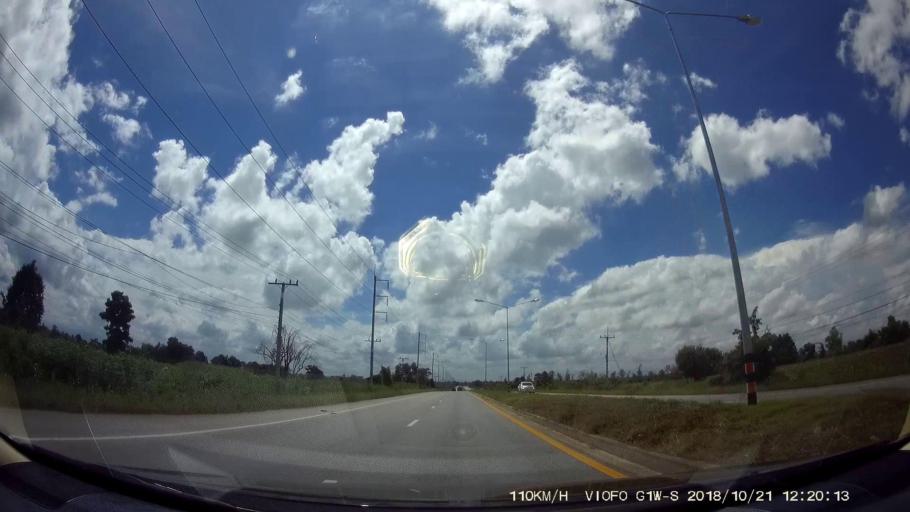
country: TH
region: Nakhon Ratchasima
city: Dan Khun Thot
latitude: 15.2907
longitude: 101.8054
